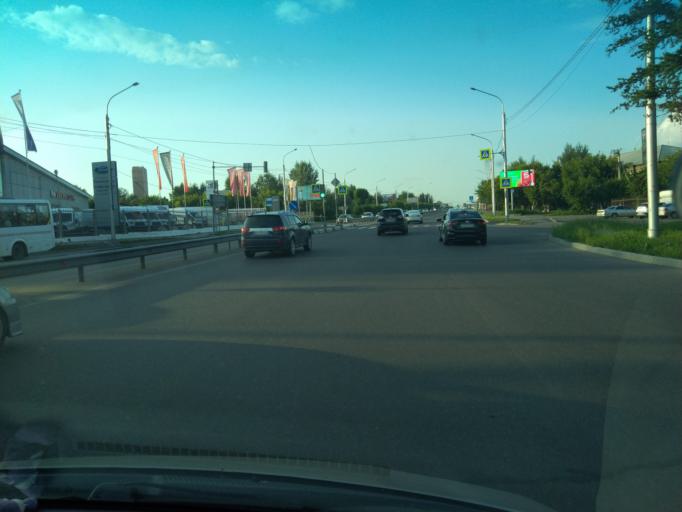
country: RU
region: Krasnoyarskiy
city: Krasnoyarsk
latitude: 56.0237
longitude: 92.8853
